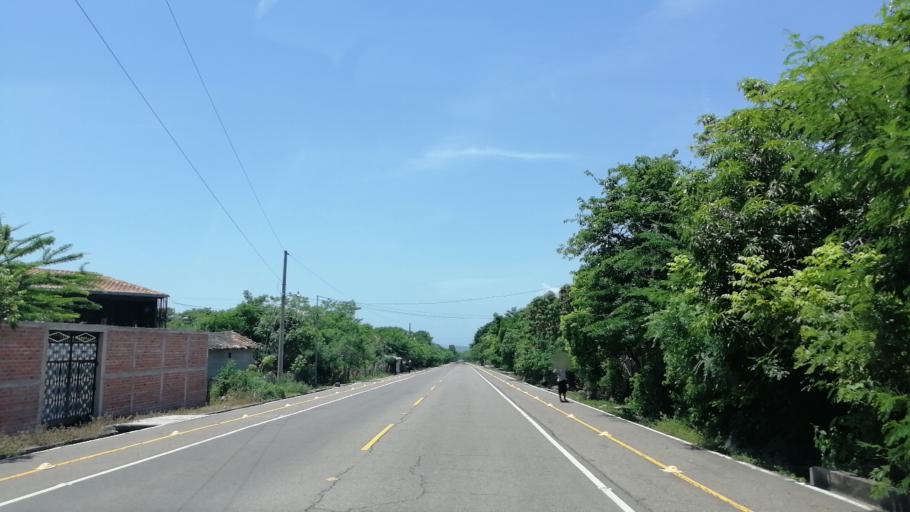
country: SV
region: Chalatenango
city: Nueva Concepcion
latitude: 14.1439
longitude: -89.3007
